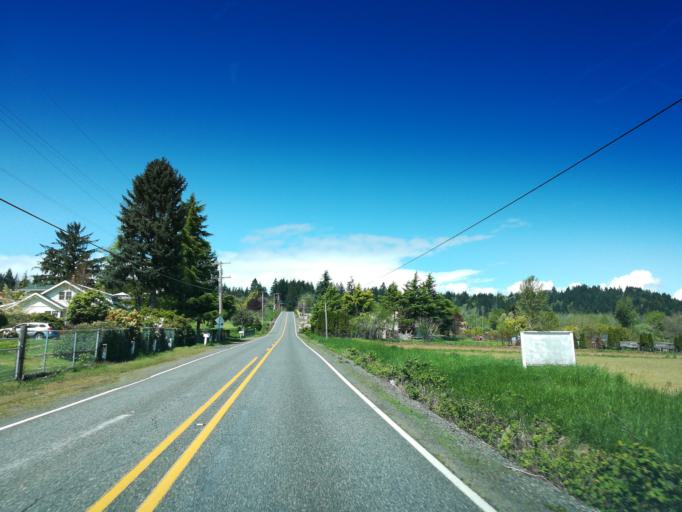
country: US
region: Oregon
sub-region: Clackamas County
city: Damascus
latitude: 45.4485
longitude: -122.4340
